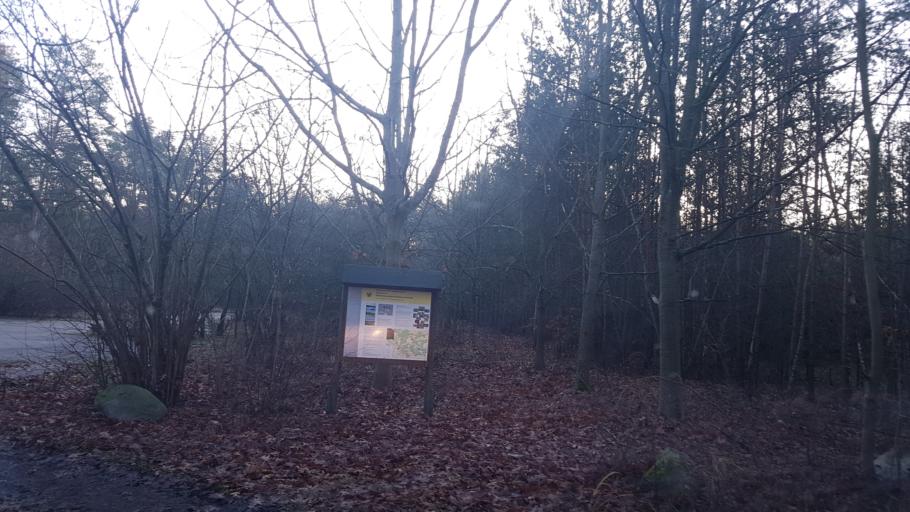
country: DE
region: Brandenburg
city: Ruckersdorf
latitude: 51.5899
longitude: 13.5872
